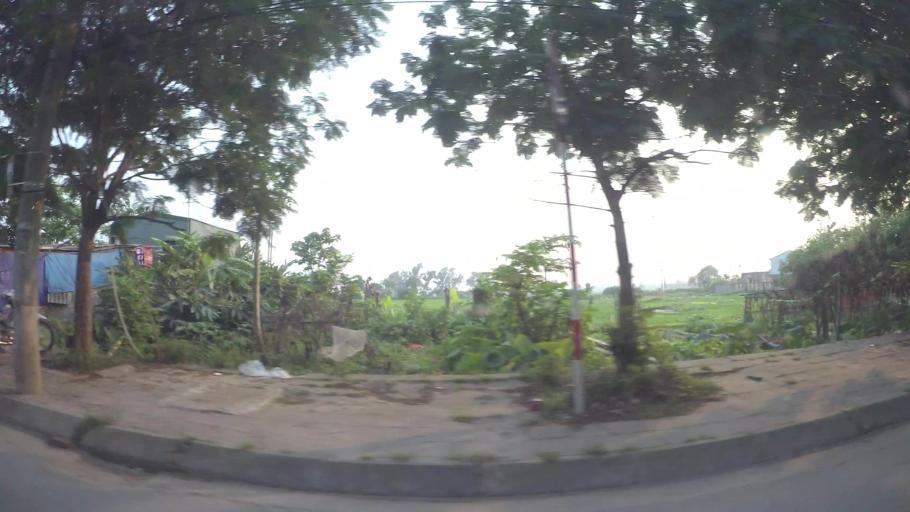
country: VN
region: Ha Noi
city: Van Dien
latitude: 20.9241
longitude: 105.8417
